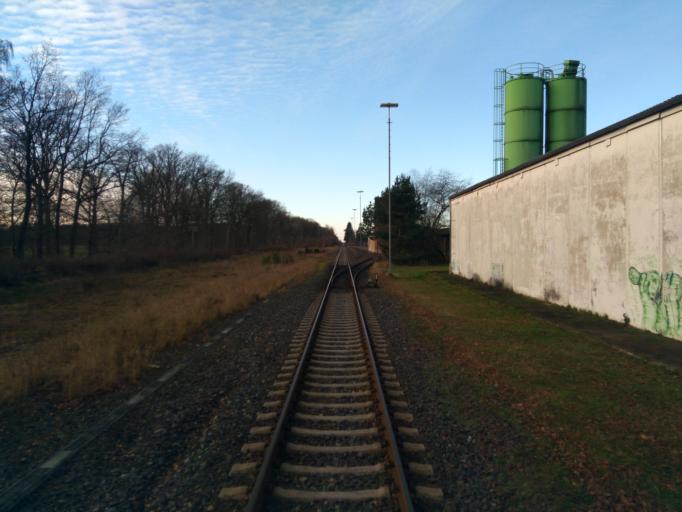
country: DE
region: Lower Saxony
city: Wriedel
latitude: 53.0021
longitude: 10.2575
